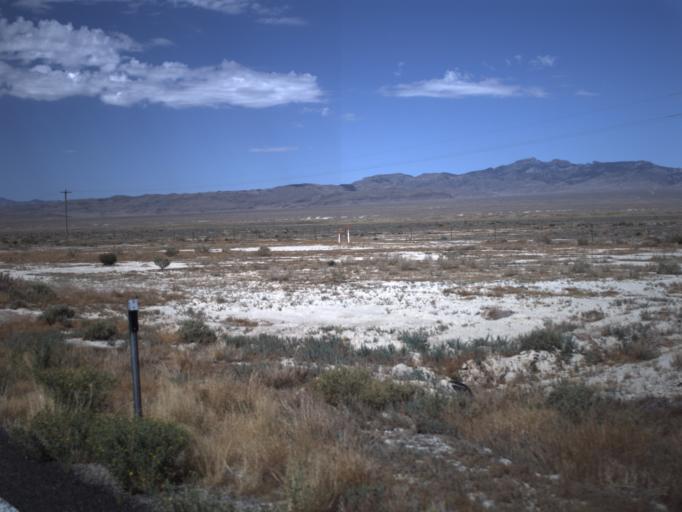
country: US
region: Utah
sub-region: Millard County
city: Delta
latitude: 39.0996
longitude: -113.1559
